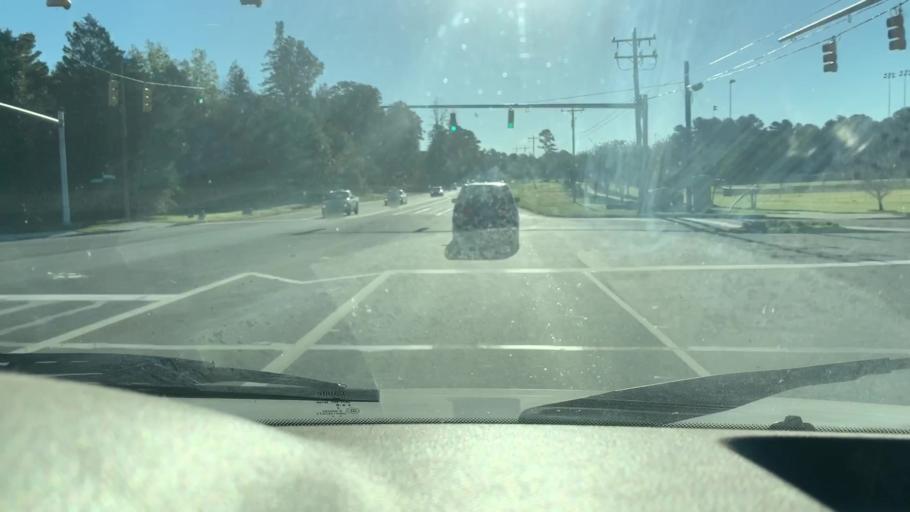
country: US
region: North Carolina
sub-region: Mecklenburg County
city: Huntersville
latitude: 35.4483
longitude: -80.7901
